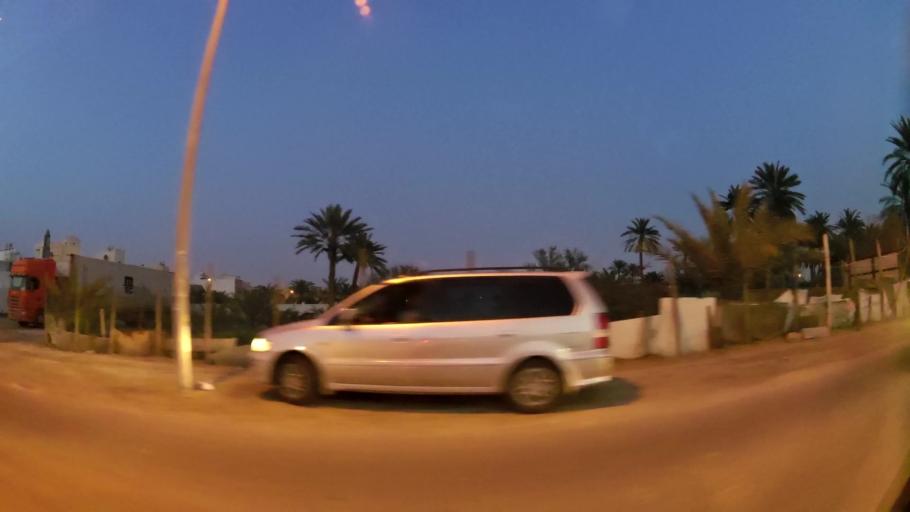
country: BH
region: Manama
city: Jidd Hafs
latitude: 26.2016
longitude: 50.5525
